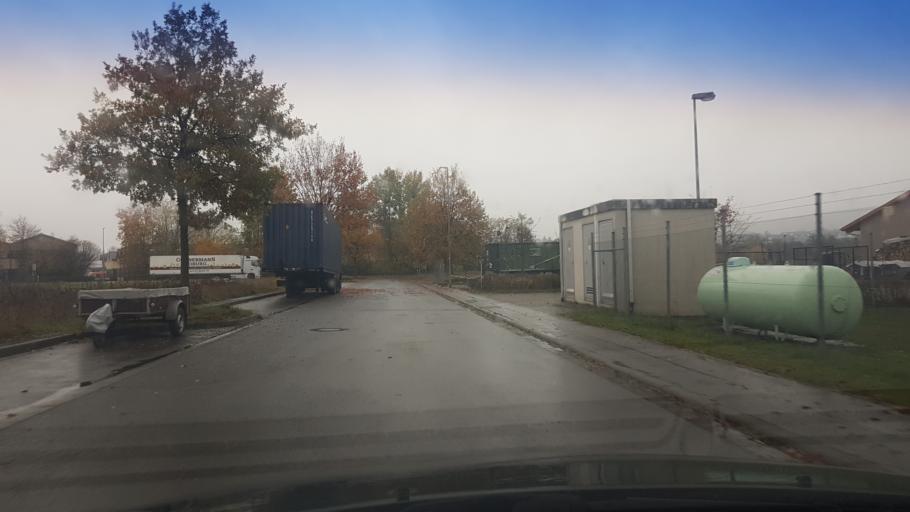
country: DE
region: Bavaria
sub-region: Upper Franconia
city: Baunach
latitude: 49.9931
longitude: 10.8514
